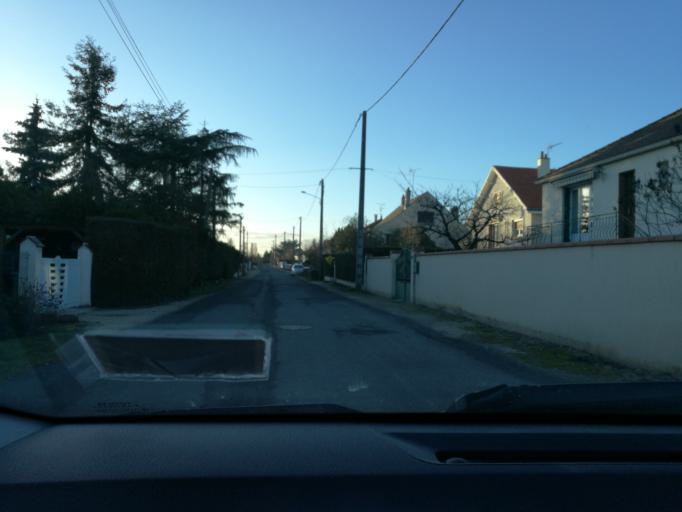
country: FR
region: Centre
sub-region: Departement du Loiret
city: Semoy
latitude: 47.9341
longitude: 1.9654
